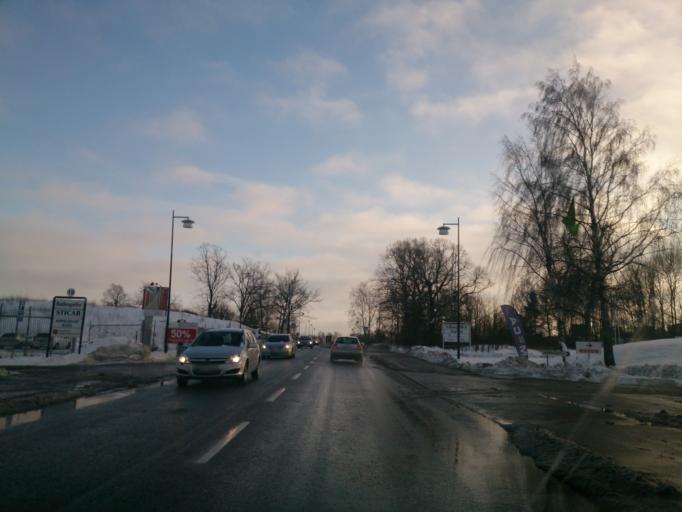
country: SE
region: OEstergoetland
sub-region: Norrkopings Kommun
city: Norrkoping
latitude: 58.6160
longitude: 16.1559
